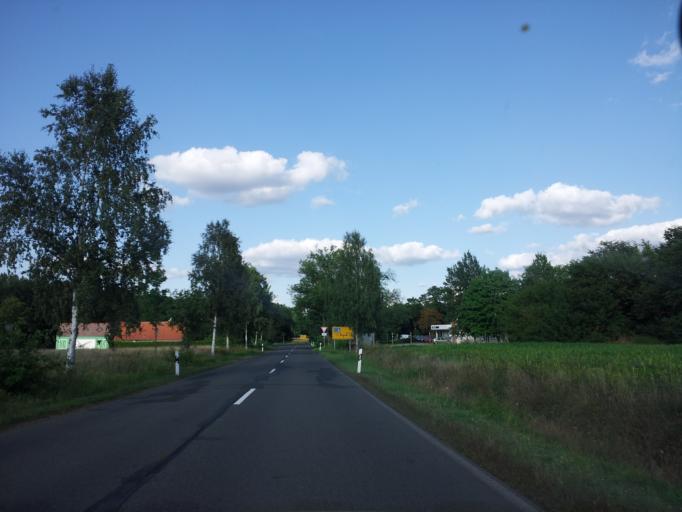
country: DE
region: Brandenburg
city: Niedergorsdorf
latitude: 52.0035
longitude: 13.0179
